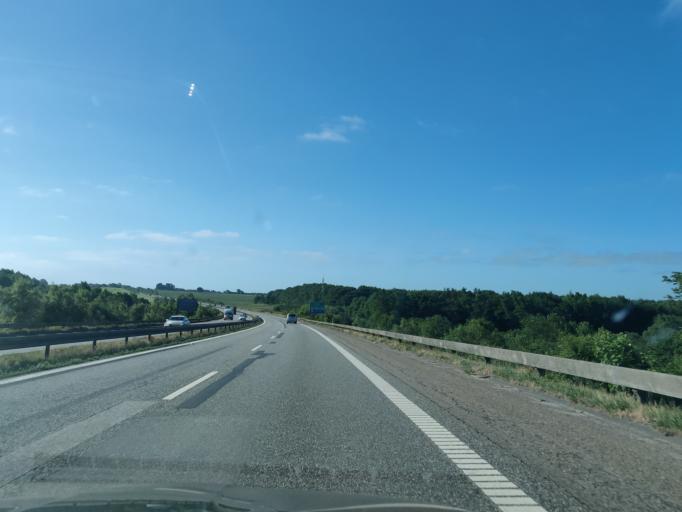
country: DK
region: North Denmark
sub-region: Mariagerfjord Kommune
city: Hobro
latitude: 56.6175
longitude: 9.7347
